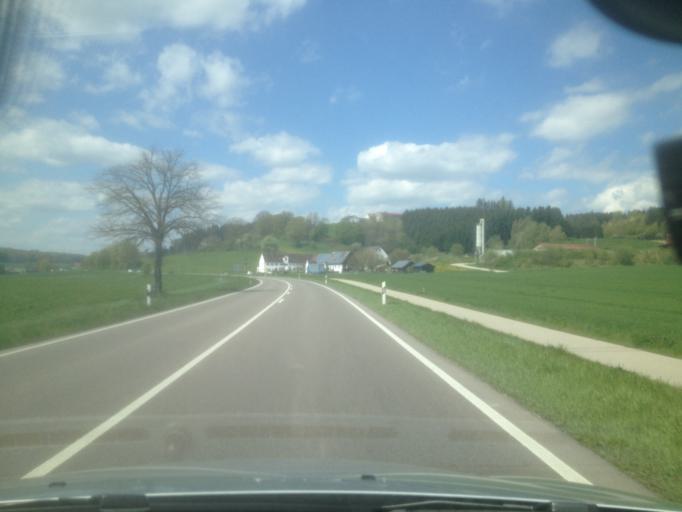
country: DE
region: Bavaria
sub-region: Swabia
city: Horgau
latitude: 48.3975
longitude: 10.6551
